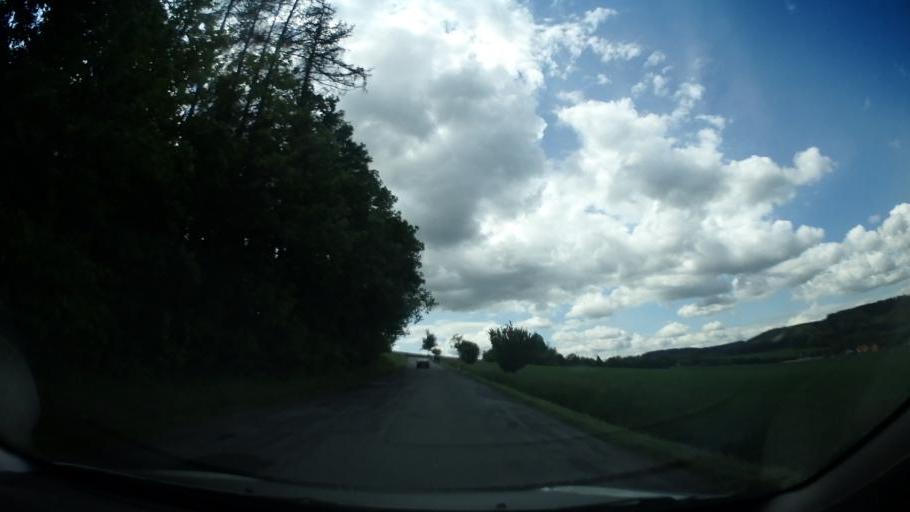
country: CZ
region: South Moravian
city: Velke Opatovice
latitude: 49.6230
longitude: 16.6104
